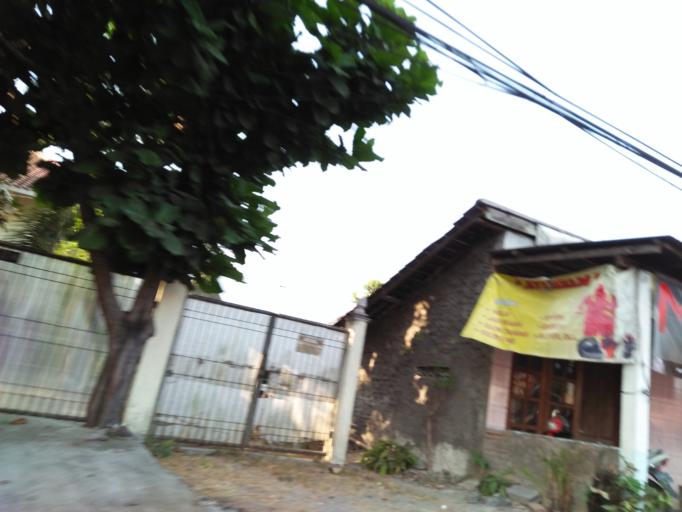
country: ID
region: Daerah Istimewa Yogyakarta
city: Depok
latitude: -7.7834
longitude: 110.4466
